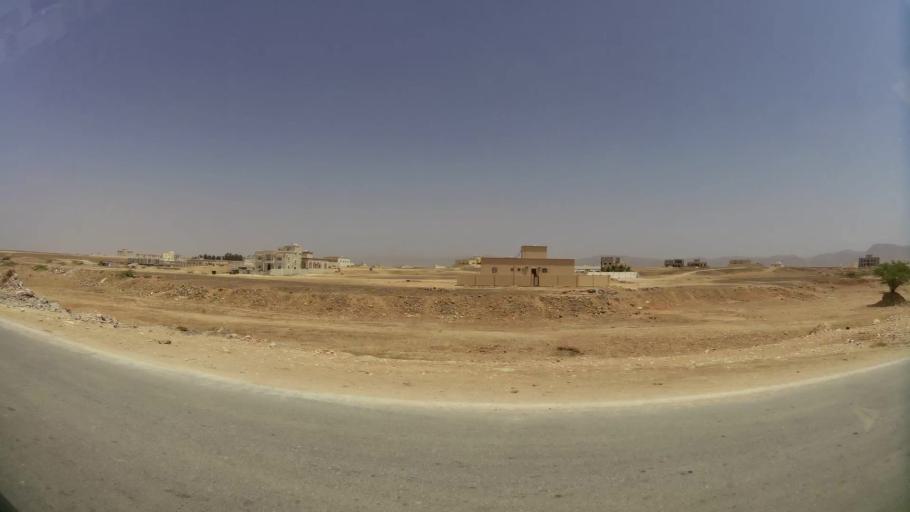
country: OM
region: Zufar
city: Salalah
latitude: 17.0863
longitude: 54.1948
